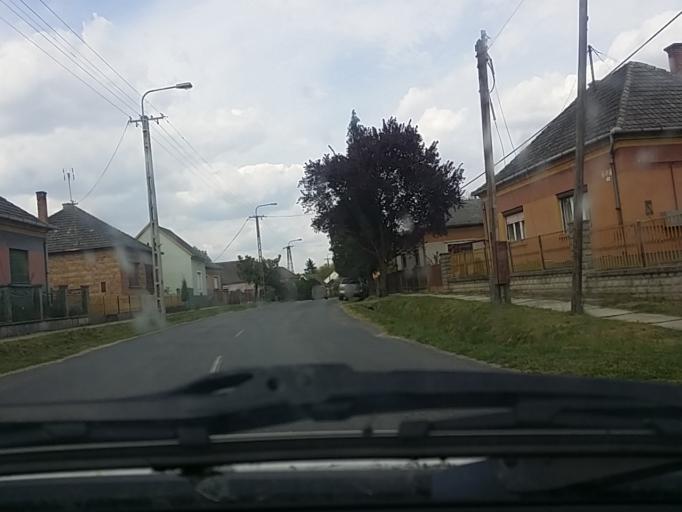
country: HR
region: Koprivnicko-Krizevacka
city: Ferdinandovac
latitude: 46.0905
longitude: 17.2289
